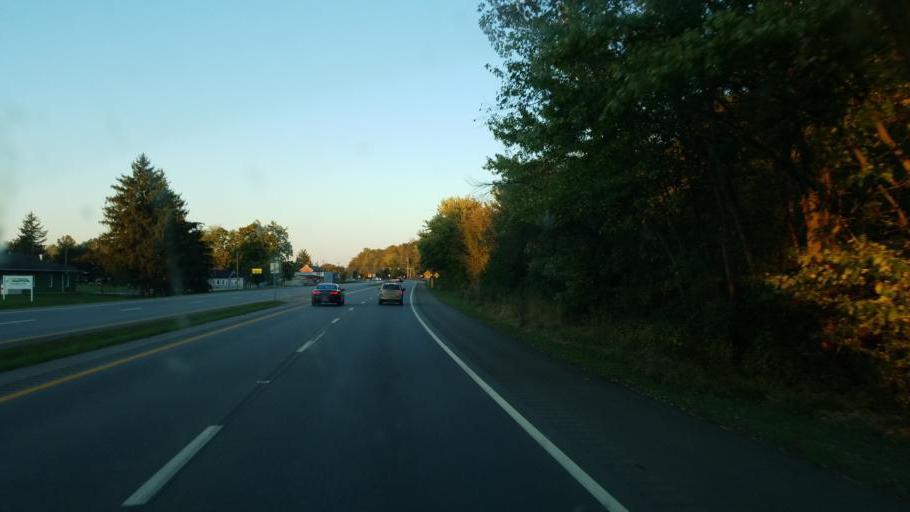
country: US
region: Ohio
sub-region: Pike County
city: Piketon
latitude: 39.0665
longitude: -83.0119
